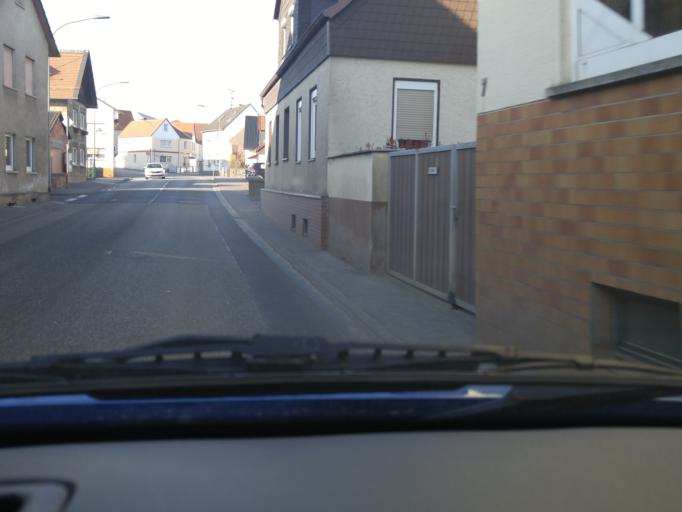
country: DE
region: Hesse
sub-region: Regierungsbezirk Darmstadt
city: Friedberg
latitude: 50.2997
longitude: 8.7517
